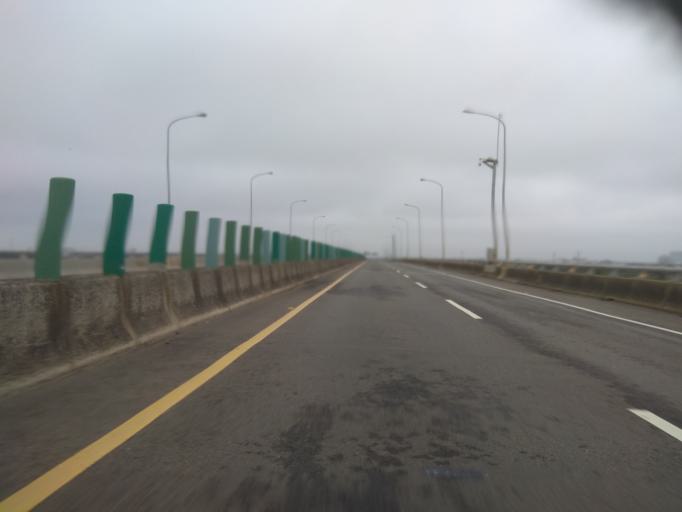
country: TW
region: Taiwan
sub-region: Hsinchu
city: Zhubei
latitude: 25.0012
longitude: 121.0992
